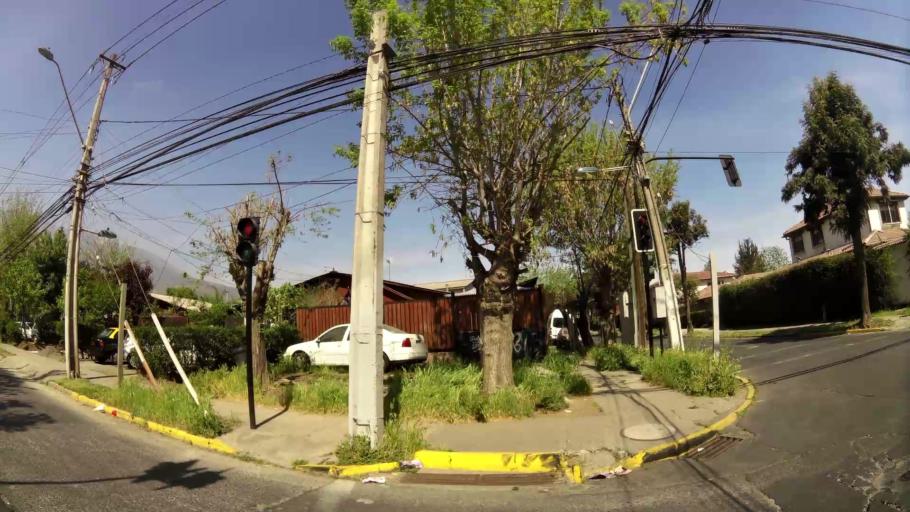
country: CL
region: Santiago Metropolitan
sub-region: Provincia de Santiago
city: Villa Presidente Frei, Nunoa, Santiago, Chile
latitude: -33.5271
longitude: -70.5657
